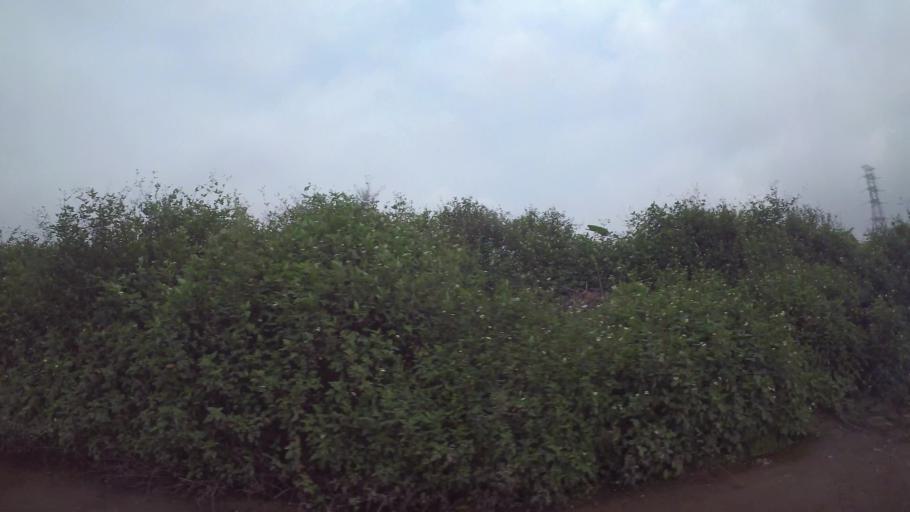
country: VN
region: Ha Noi
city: Van Dien
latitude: 20.9756
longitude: 105.8631
